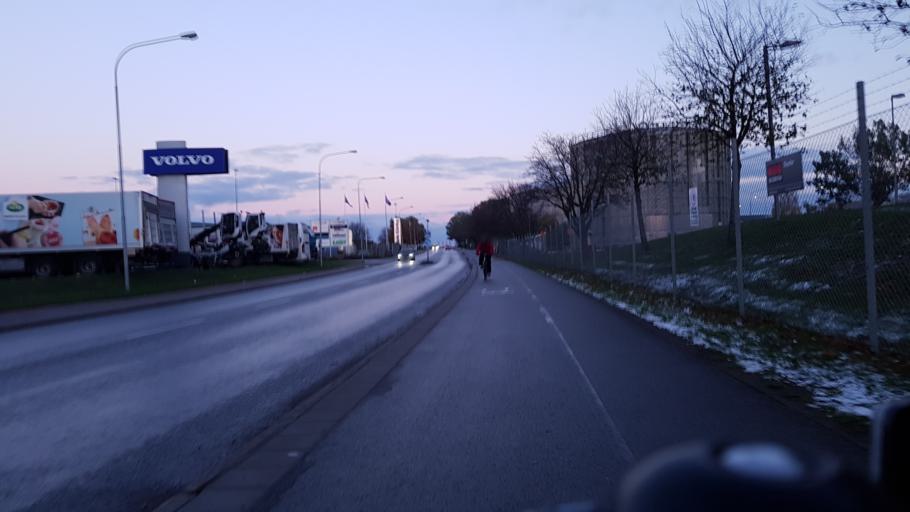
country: SE
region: Uppsala
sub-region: Uppsala Kommun
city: Uppsala
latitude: 59.8539
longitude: 17.6749
